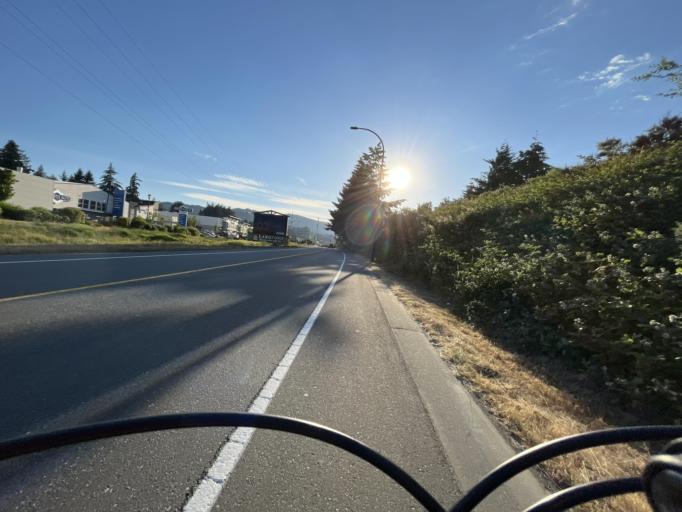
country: CA
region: British Columbia
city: Langford
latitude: 48.4434
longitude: -123.5169
